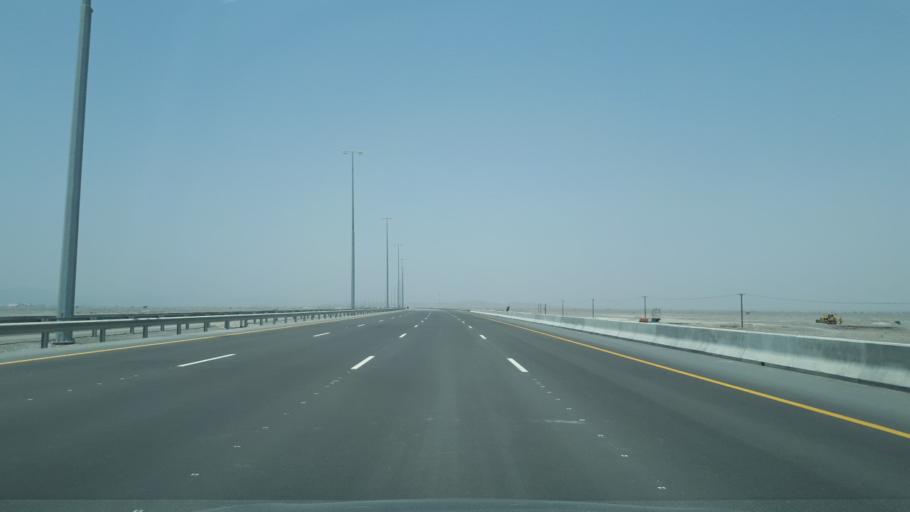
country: OM
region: Al Batinah
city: Barka'
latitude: 23.5668
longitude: 57.7059
